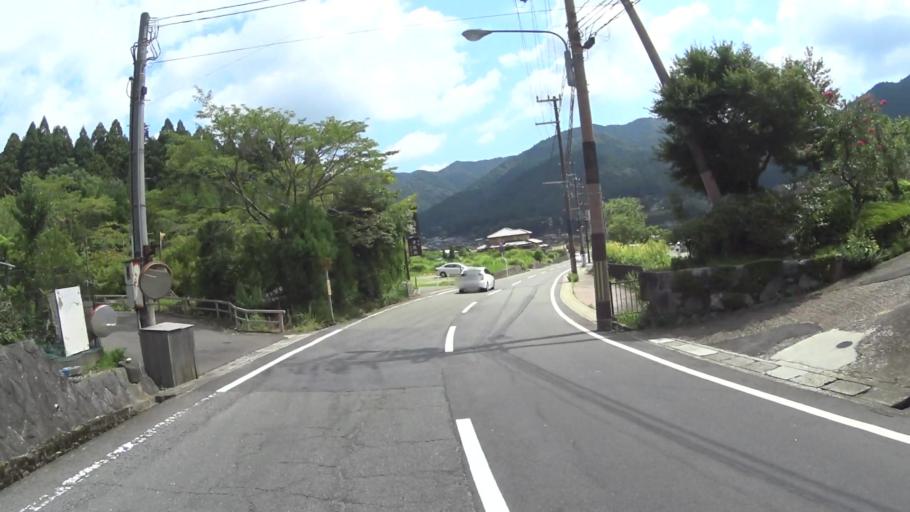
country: JP
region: Kyoto
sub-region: Kyoto-shi
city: Kamigyo-ku
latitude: 35.1115
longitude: 135.8183
